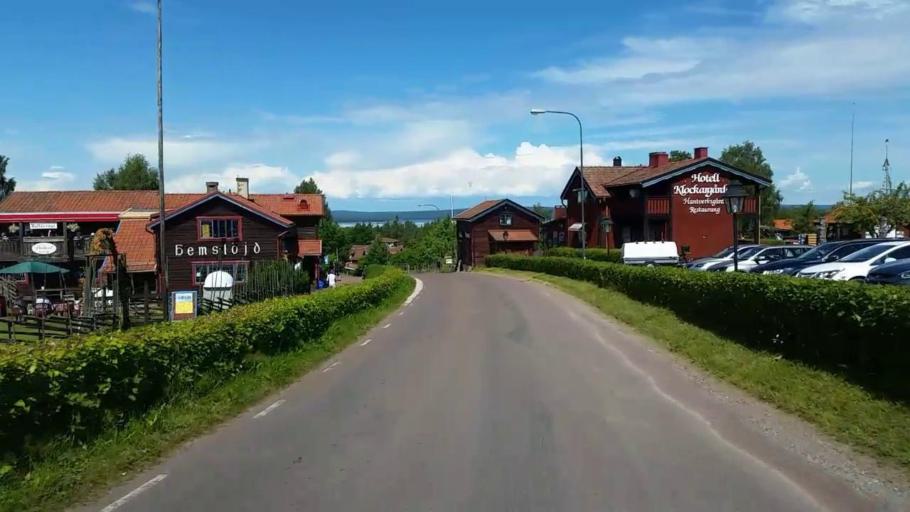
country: SE
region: Dalarna
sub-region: Leksand Municipality
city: Leksand
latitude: 60.8246
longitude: 14.9929
